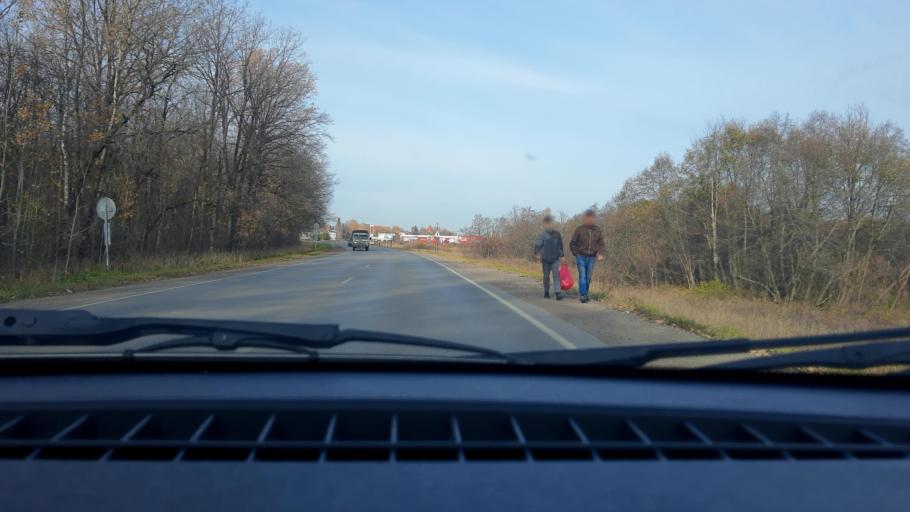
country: RU
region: Bashkortostan
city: Mikhaylovka
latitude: 54.8076
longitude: 55.8192
